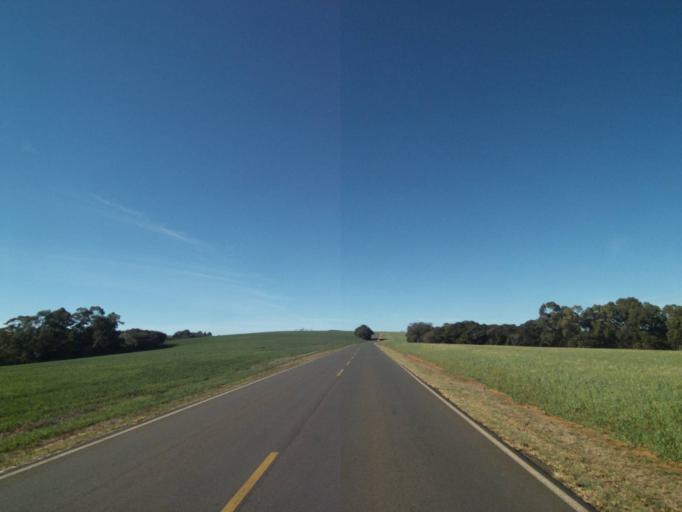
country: BR
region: Parana
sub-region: Tibagi
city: Tibagi
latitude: -24.5327
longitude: -50.3172
